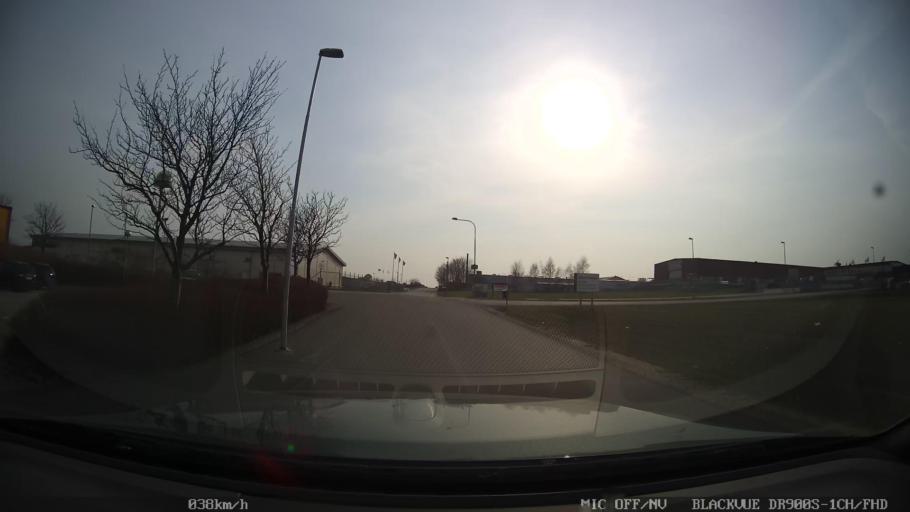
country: SE
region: Skane
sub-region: Ystads Kommun
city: Ystad
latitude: 55.4491
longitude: 13.8473
